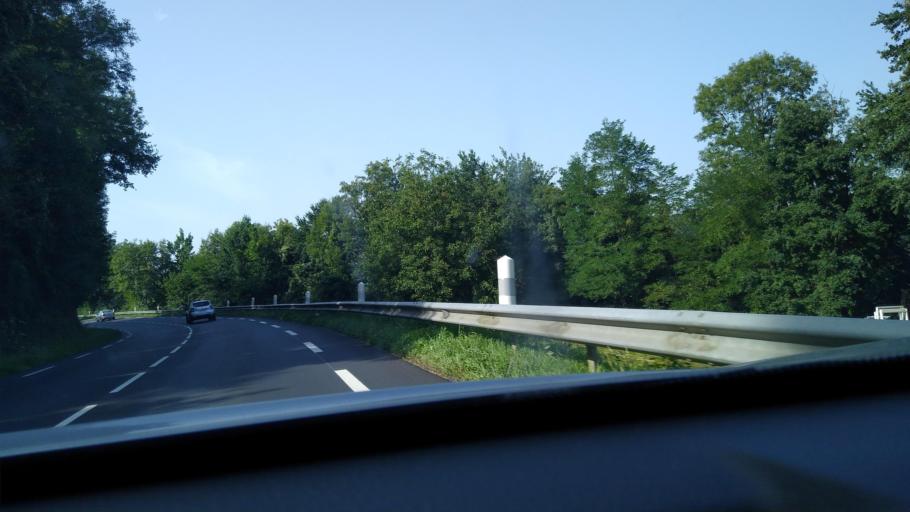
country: FR
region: Midi-Pyrenees
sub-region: Departement de la Haute-Garonne
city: Salies-du-Salat
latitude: 43.0711
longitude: 0.9664
